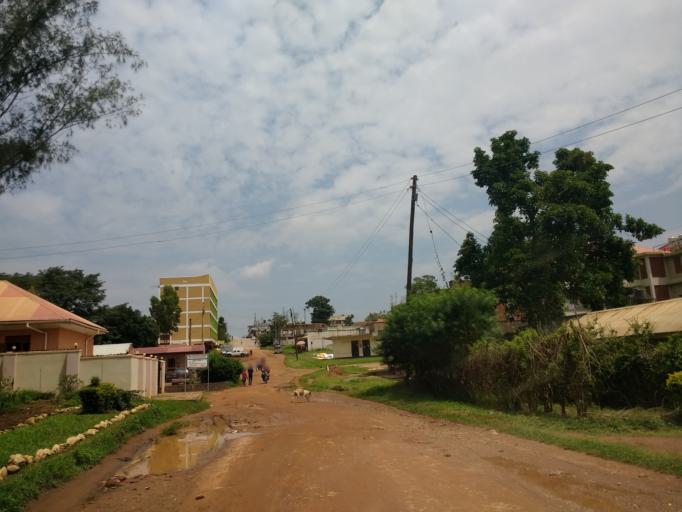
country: UG
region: Eastern Region
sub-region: Mbale District
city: Mbale
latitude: 1.0752
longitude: 34.1821
